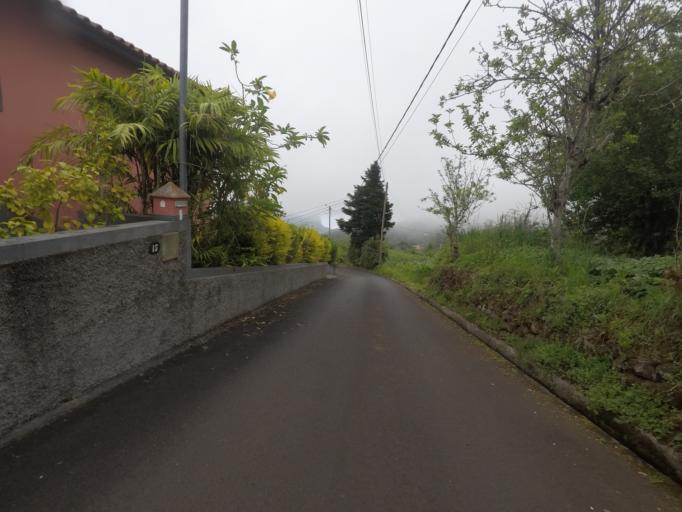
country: PT
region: Madeira
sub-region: Santana
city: Santana
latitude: 32.7474
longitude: -16.8791
